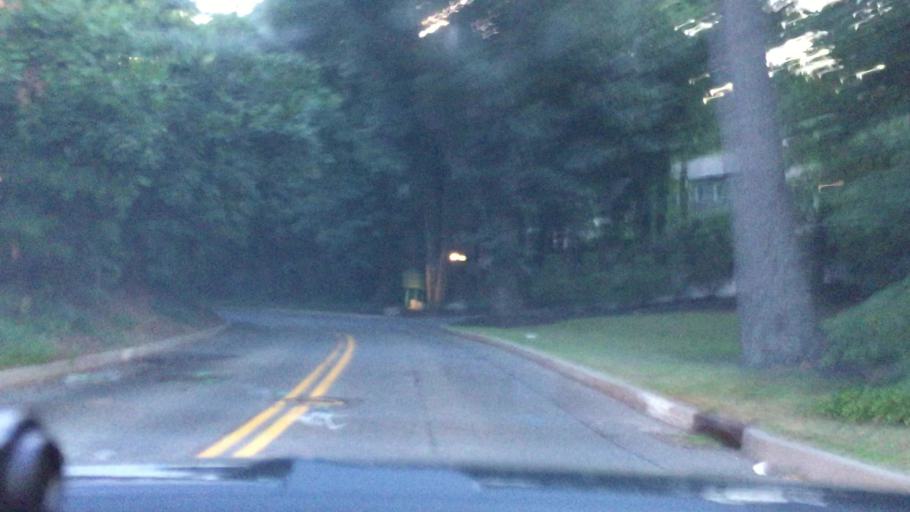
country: US
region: New York
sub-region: Suffolk County
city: Port Jefferson Station
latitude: 40.9383
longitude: -73.0555
